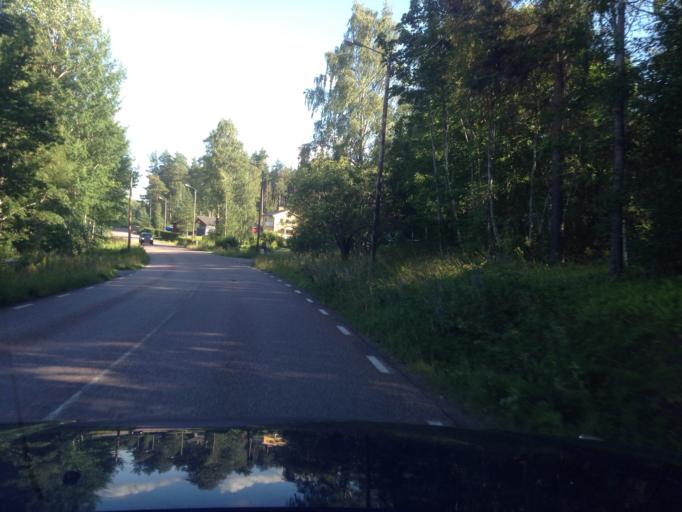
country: SE
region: Dalarna
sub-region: Ludvika Kommun
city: Grangesberg
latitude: 60.2093
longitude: 14.9595
